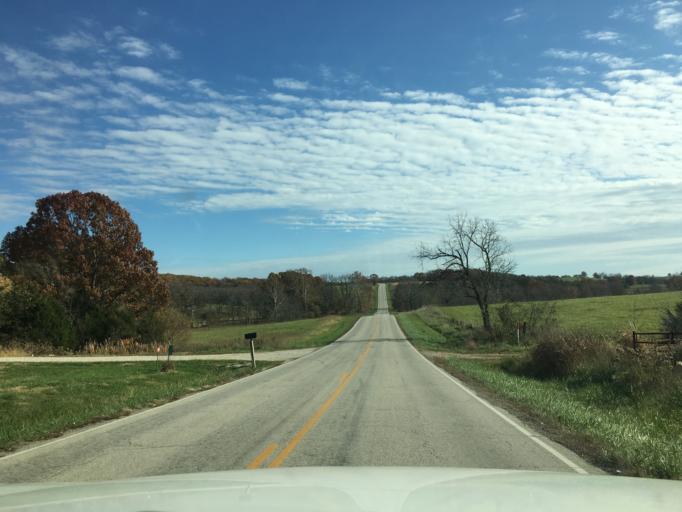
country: US
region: Missouri
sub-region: Maries County
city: Belle
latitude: 38.3397
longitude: -91.7856
